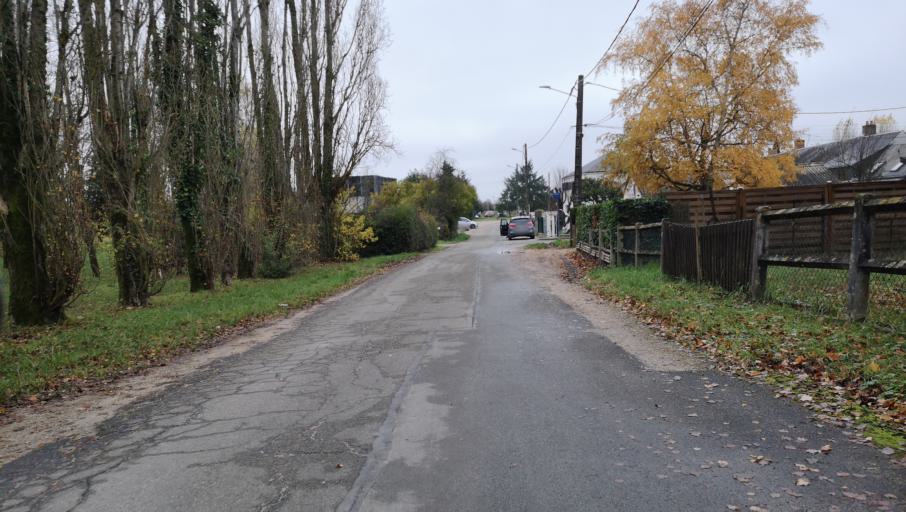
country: FR
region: Centre
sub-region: Departement du Loiret
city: Semoy
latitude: 47.9270
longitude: 1.9639
